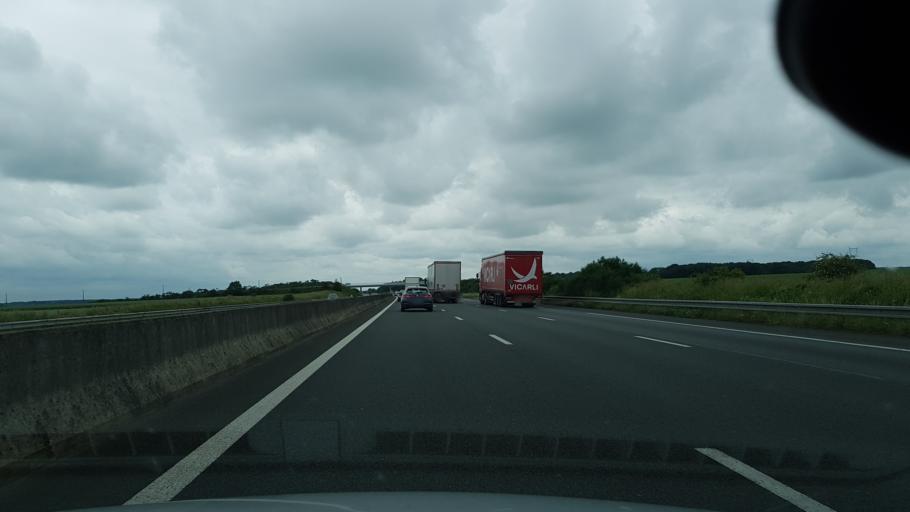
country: FR
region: Centre
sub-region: Departement du Loir-et-Cher
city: Herbault
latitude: 47.5821
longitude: 1.0699
